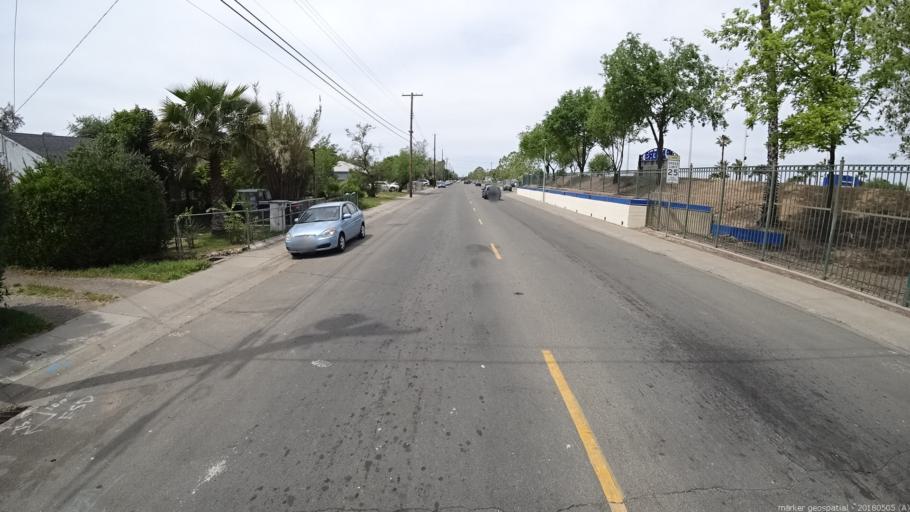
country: US
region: California
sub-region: Sacramento County
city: Rio Linda
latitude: 38.6329
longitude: -121.4325
